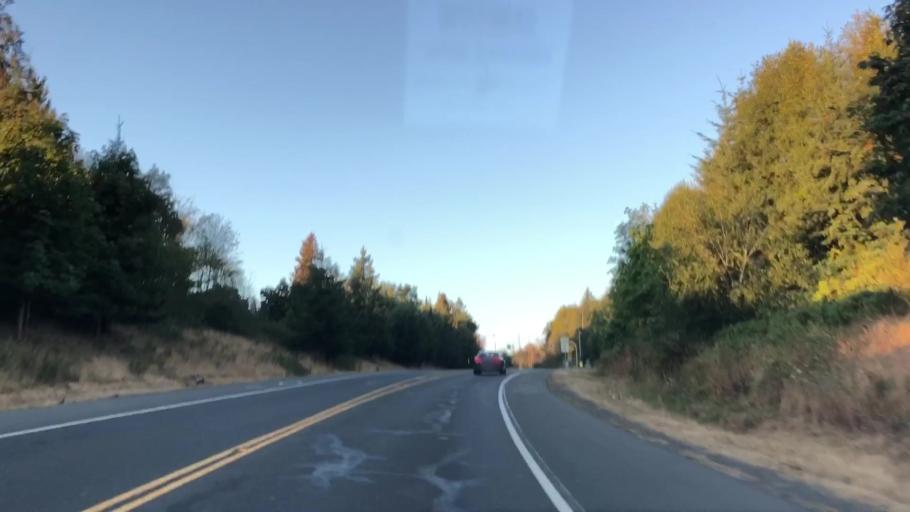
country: CA
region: British Columbia
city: Colwood
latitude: 48.4232
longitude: -123.5030
